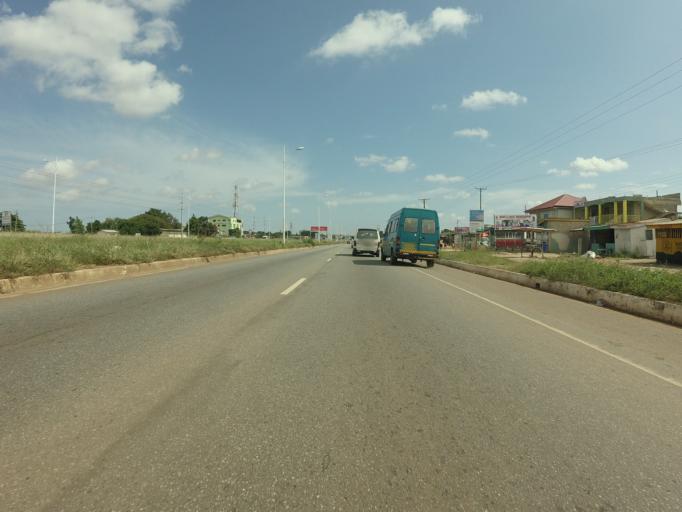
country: GH
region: Greater Accra
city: Medina Estates
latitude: 5.7130
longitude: -0.1718
